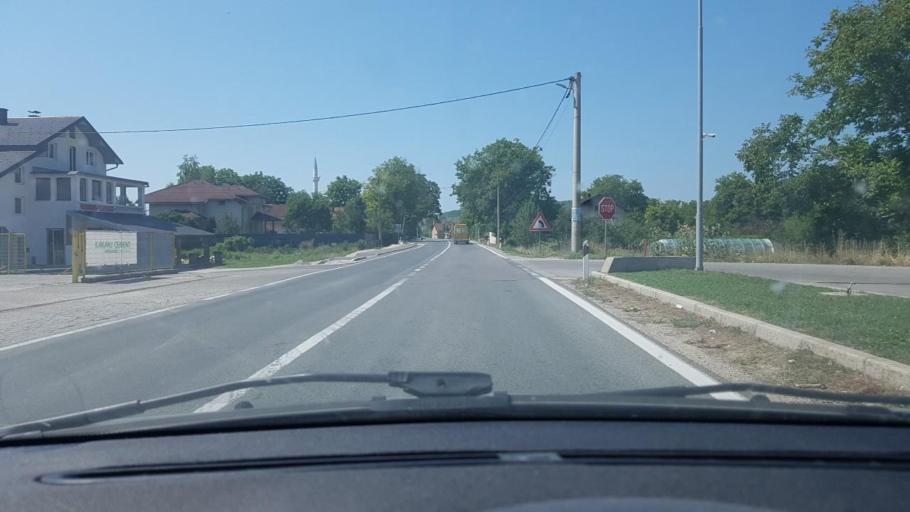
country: BA
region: Federation of Bosnia and Herzegovina
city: Bihac
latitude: 44.7896
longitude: 15.9297
